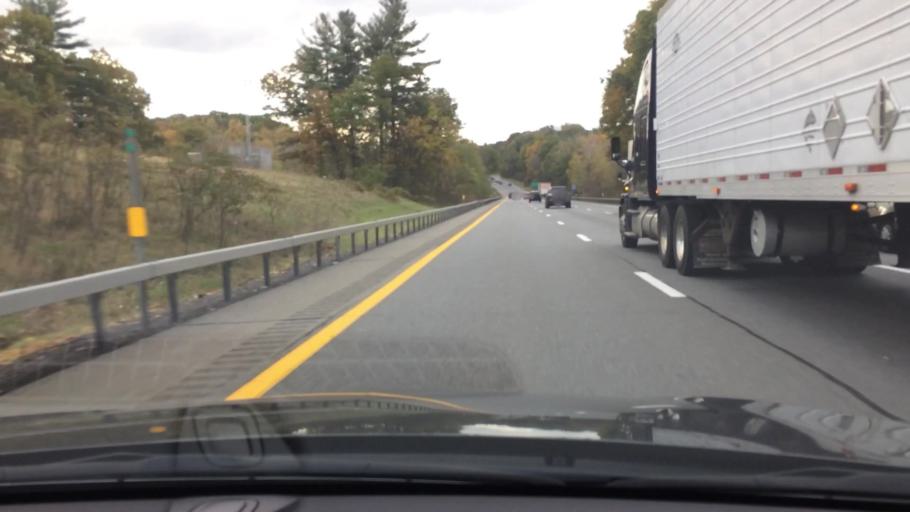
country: US
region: New York
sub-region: Saratoga County
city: Country Knolls
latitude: 42.9309
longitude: -73.8036
